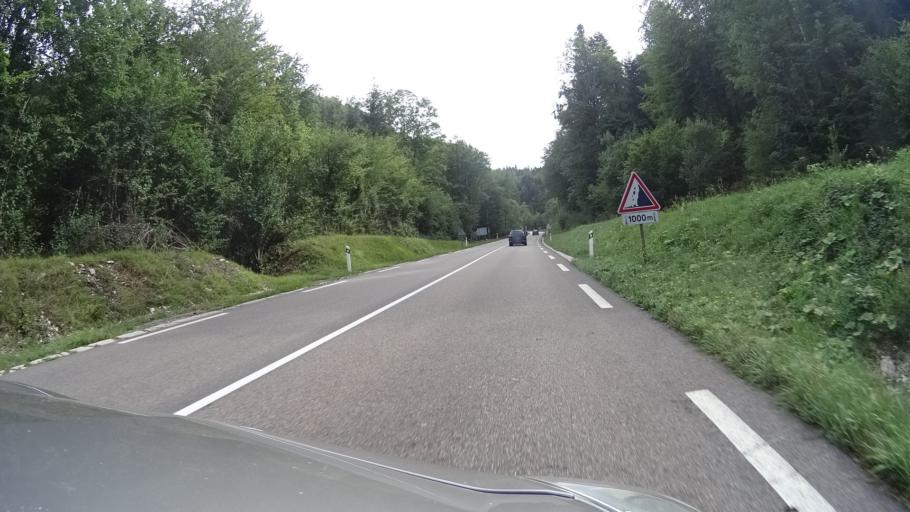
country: FR
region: Franche-Comte
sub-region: Departement du Jura
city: Champagnole
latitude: 46.6715
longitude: 5.9386
